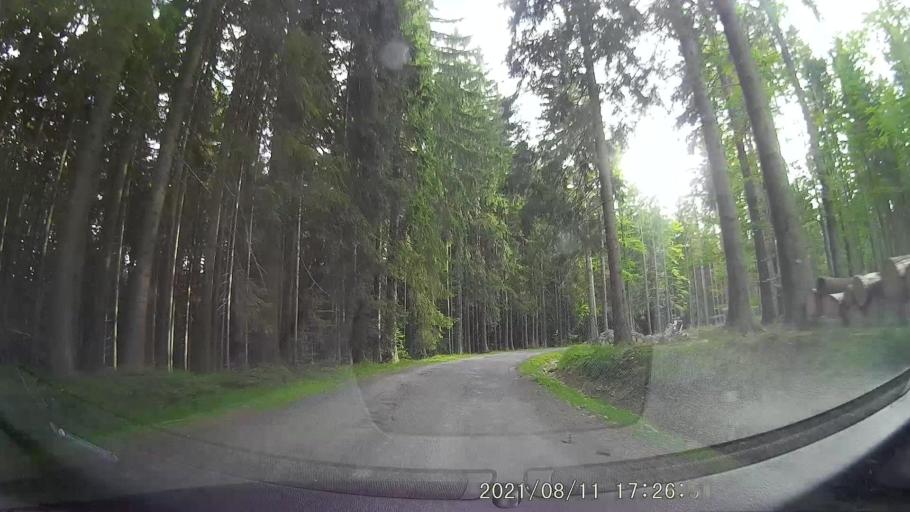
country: PL
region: Lower Silesian Voivodeship
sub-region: Powiat klodzki
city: Polanica-Zdroj
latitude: 50.3016
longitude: 16.4959
